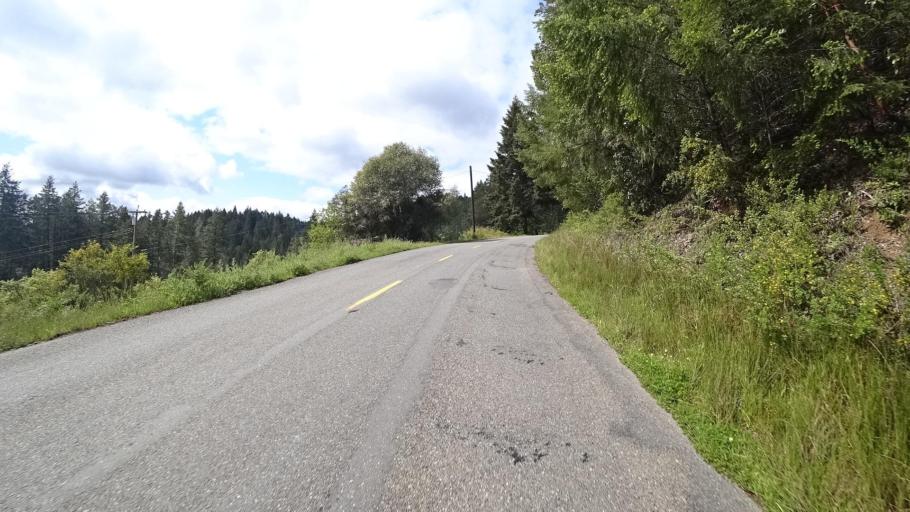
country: US
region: California
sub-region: Humboldt County
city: Redway
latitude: 40.1490
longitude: -123.6268
